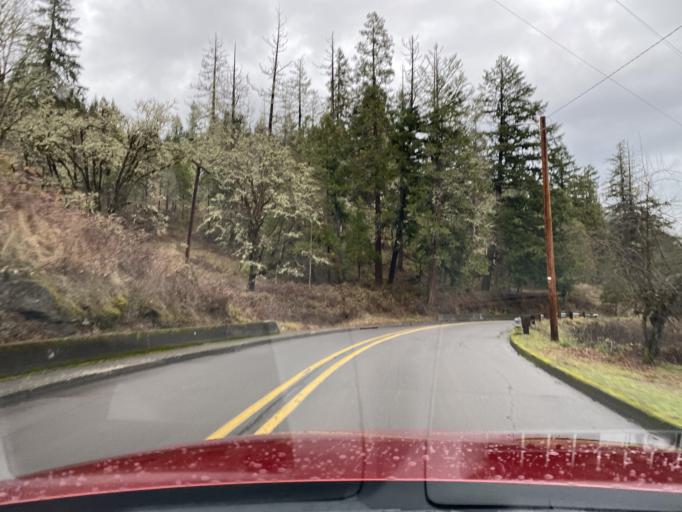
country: US
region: Oregon
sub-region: Lane County
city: Oakridge
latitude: 43.7518
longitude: -122.4865
